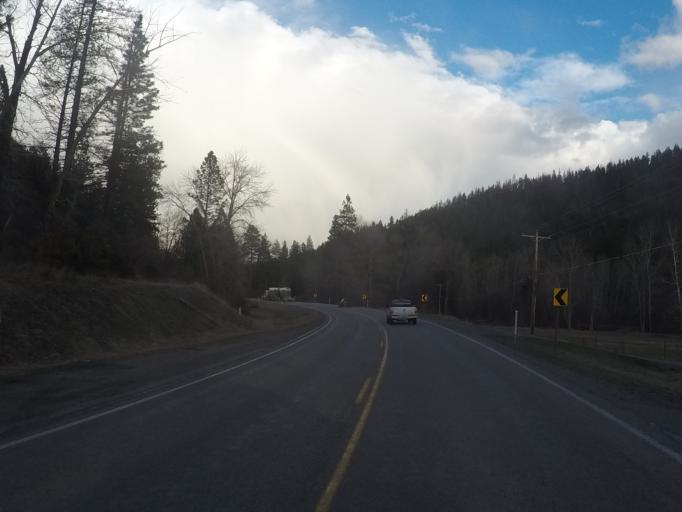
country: US
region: Montana
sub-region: Missoula County
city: Lolo
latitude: 46.7433
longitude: -114.1531
